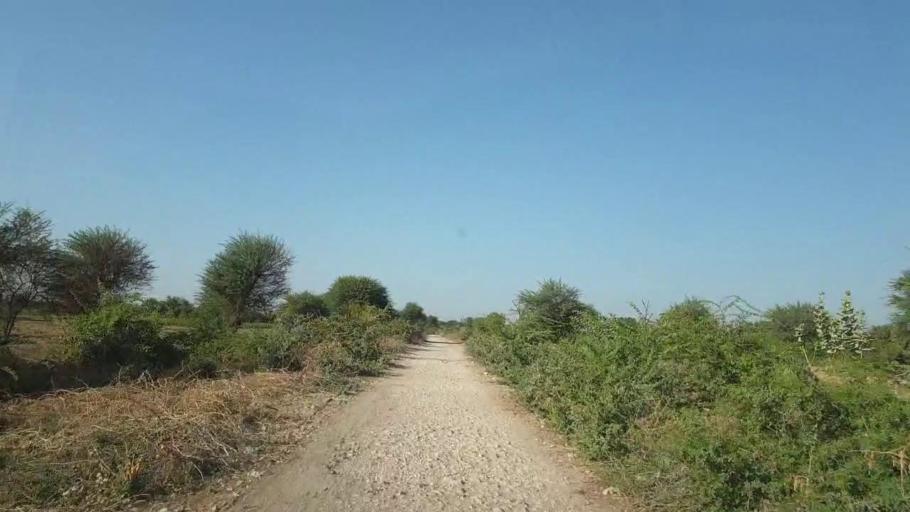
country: PK
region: Sindh
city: Kunri
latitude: 25.0585
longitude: 69.4420
